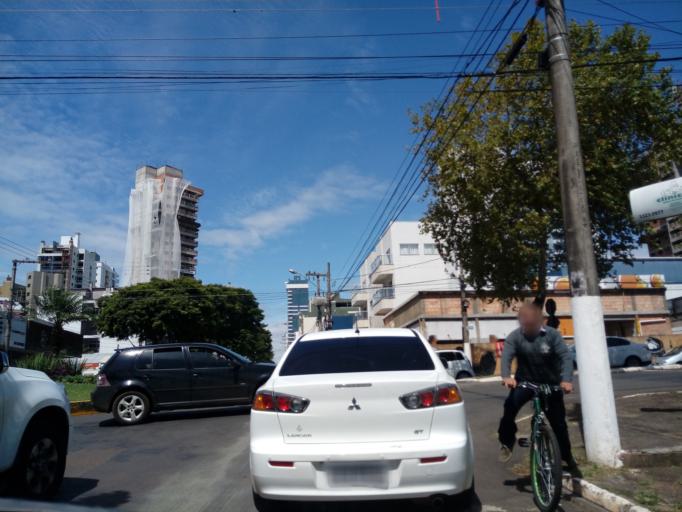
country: BR
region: Santa Catarina
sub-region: Chapeco
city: Chapeco
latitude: -27.0995
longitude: -52.6122
